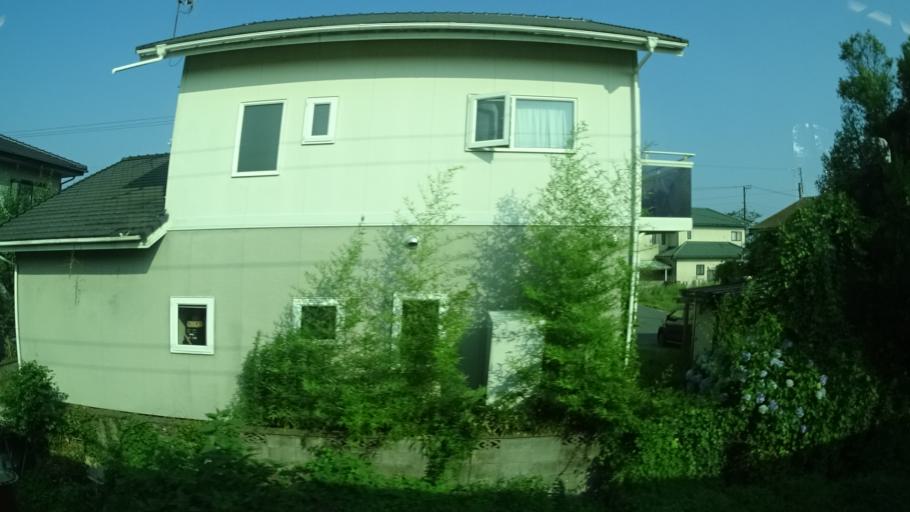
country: JP
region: Ibaraki
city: Kitaibaraki
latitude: 36.8241
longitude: 140.7719
